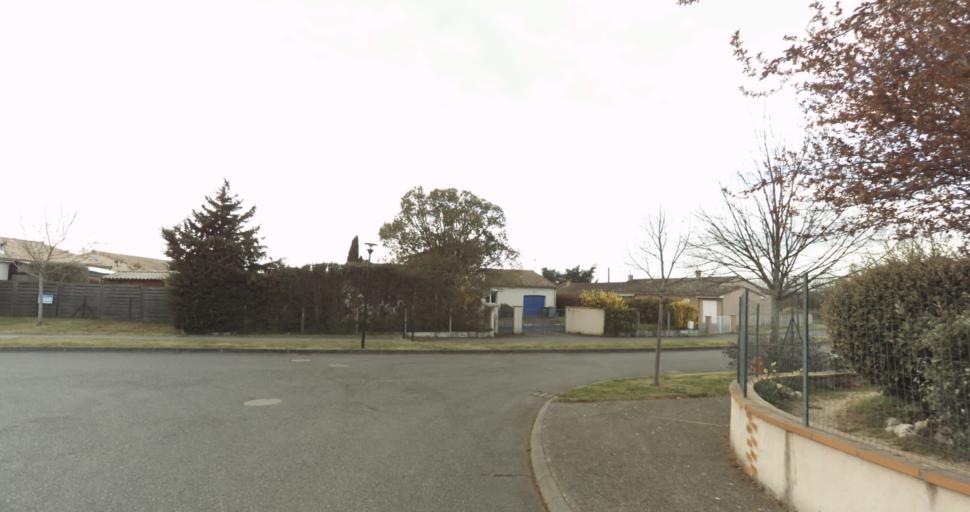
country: FR
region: Midi-Pyrenees
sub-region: Departement de la Haute-Garonne
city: Auterive
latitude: 43.3545
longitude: 1.4832
